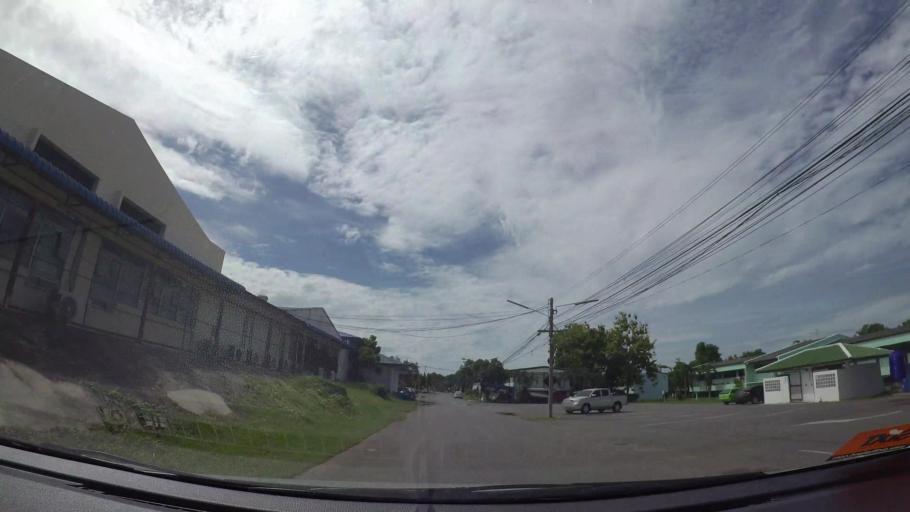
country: TH
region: Chon Buri
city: Sattahip
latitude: 12.6654
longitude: 100.9170
